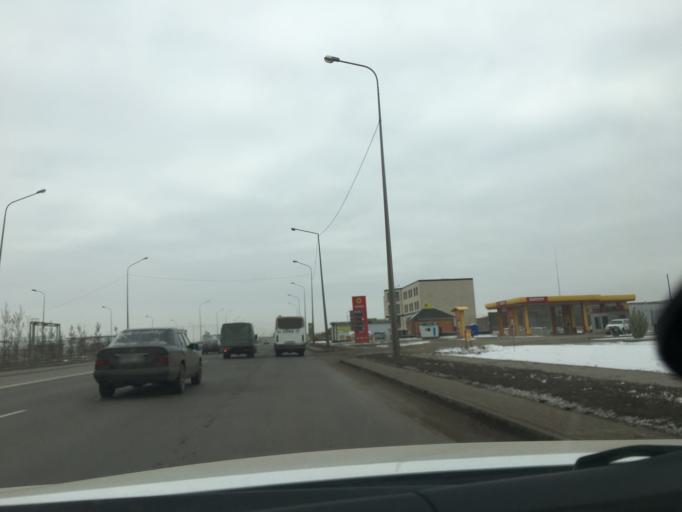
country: KZ
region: Astana Qalasy
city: Astana
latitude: 51.1597
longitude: 71.5204
